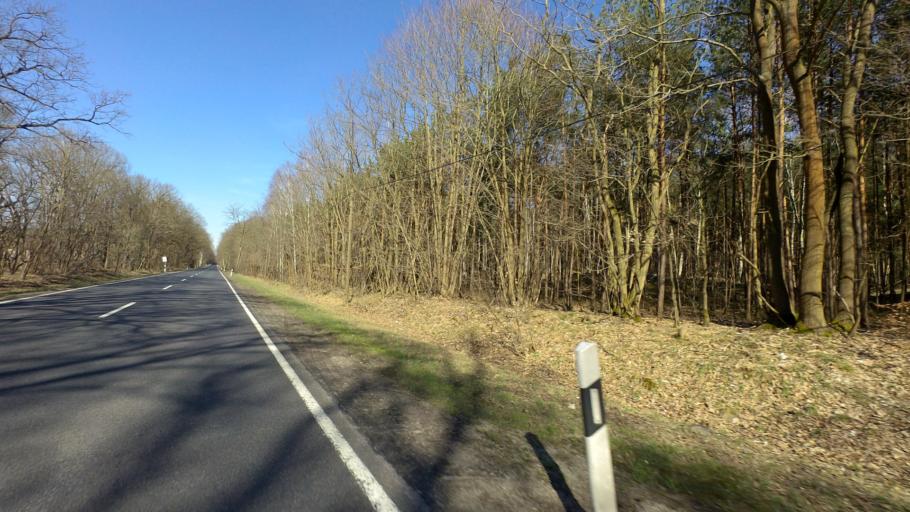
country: DE
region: Brandenburg
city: Chorin
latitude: 52.9022
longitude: 13.8896
